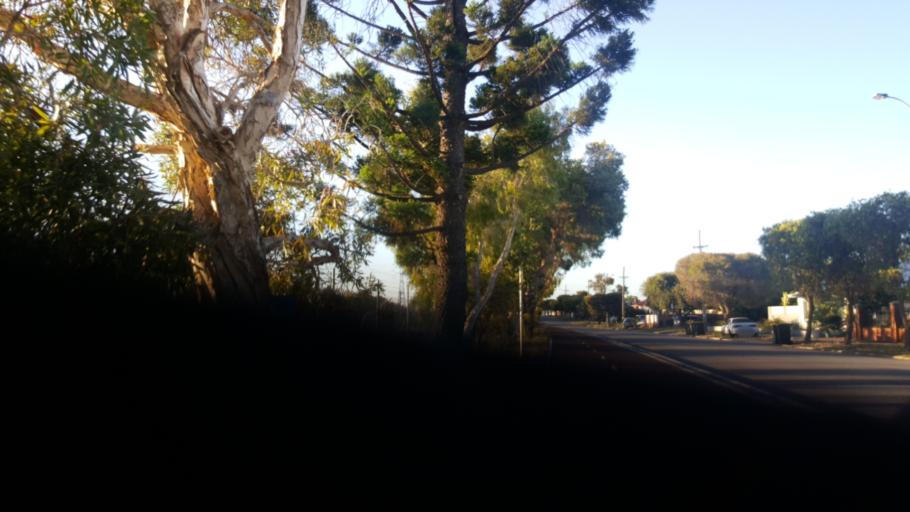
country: AU
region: Western Australia
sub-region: Victoria Park
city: East Victoria Park
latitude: -31.9850
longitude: 115.9150
